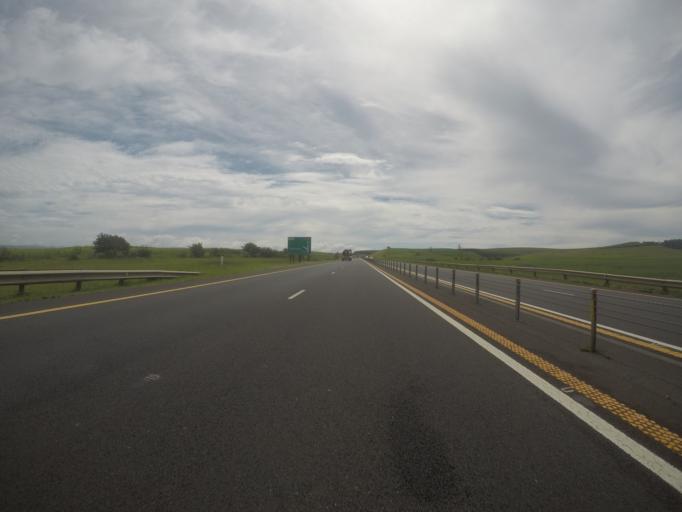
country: ZA
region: KwaZulu-Natal
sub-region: uThungulu District Municipality
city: Eshowe
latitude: -29.0526
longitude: 31.6348
